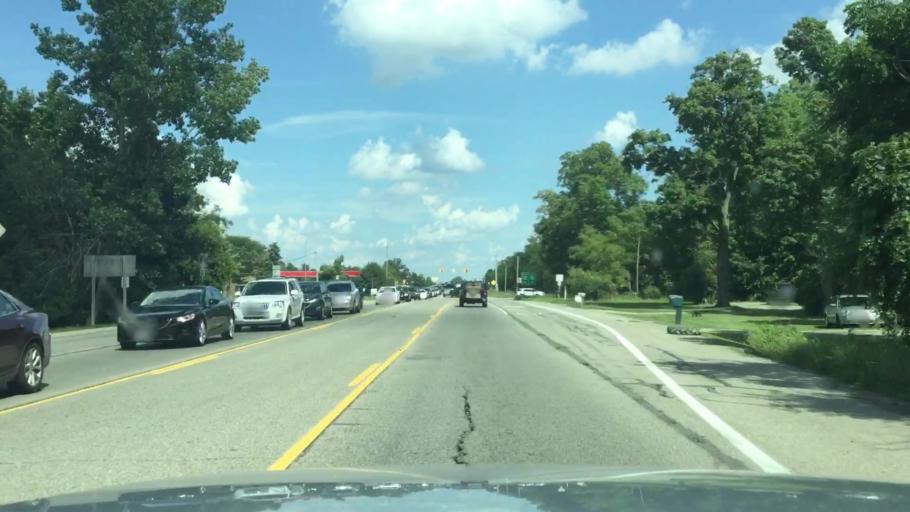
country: US
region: Michigan
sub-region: Washtenaw County
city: Ypsilanti
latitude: 42.2036
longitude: -83.6897
